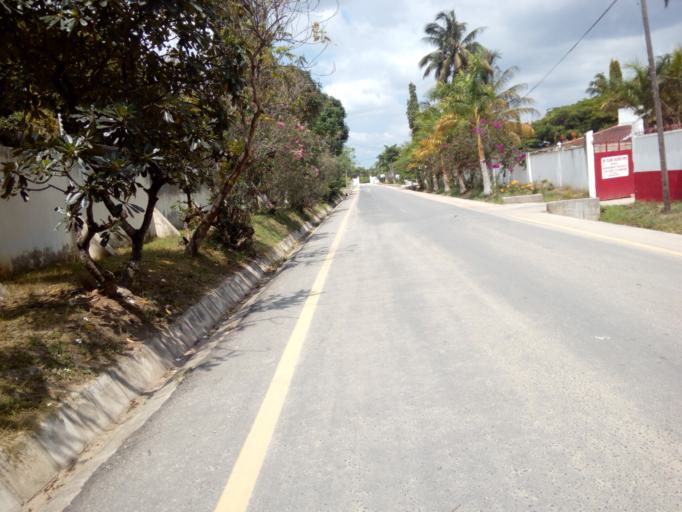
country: TZ
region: Dar es Salaam
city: Magomeni
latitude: -6.7443
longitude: 39.2360
